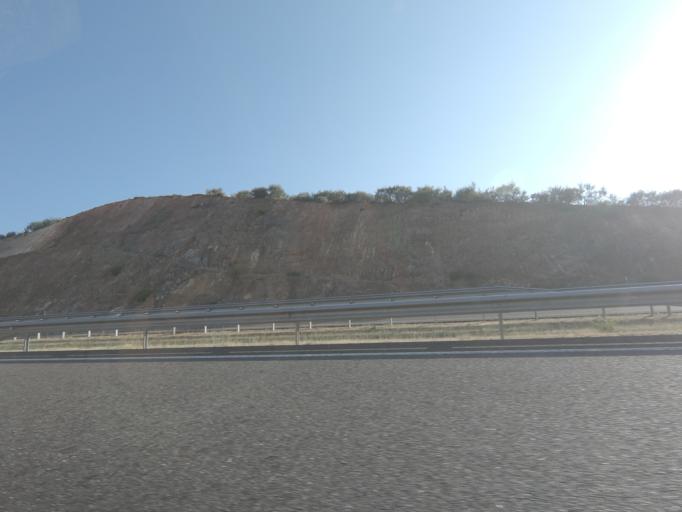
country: ES
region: Galicia
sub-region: Provincia de Ourense
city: Oimbra
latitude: 41.8573
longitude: -7.4239
